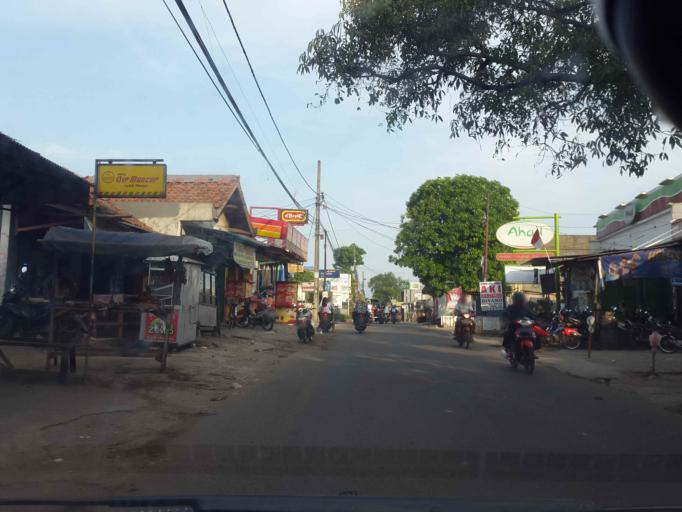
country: ID
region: West Java
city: Ciputat
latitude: -6.2444
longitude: 106.6950
